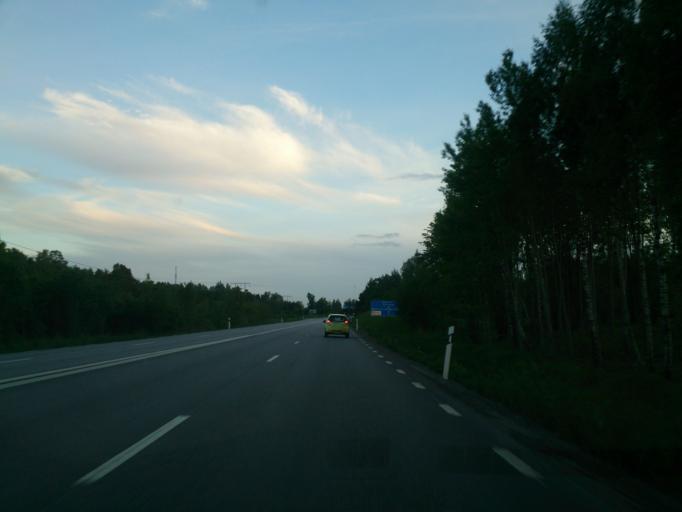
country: SE
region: OEstergoetland
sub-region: Linkopings Kommun
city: Malmslatt
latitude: 58.3973
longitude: 15.5497
